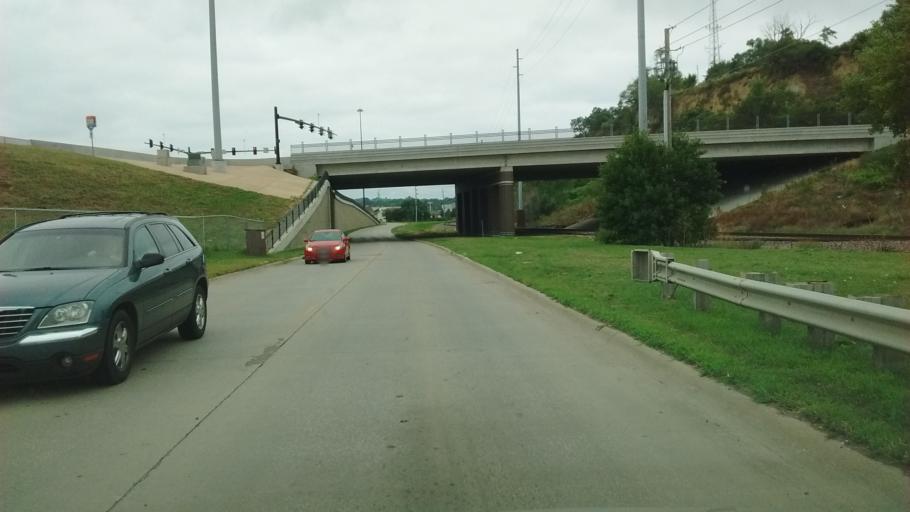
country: US
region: Iowa
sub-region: Woodbury County
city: Sioux City
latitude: 42.4918
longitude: -96.4113
